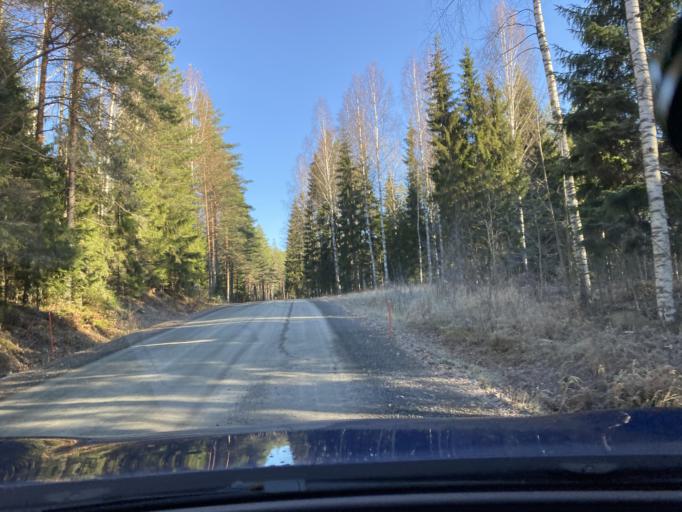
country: FI
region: Haeme
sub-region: Haemeenlinna
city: Kalvola
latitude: 60.9926
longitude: 24.0886
